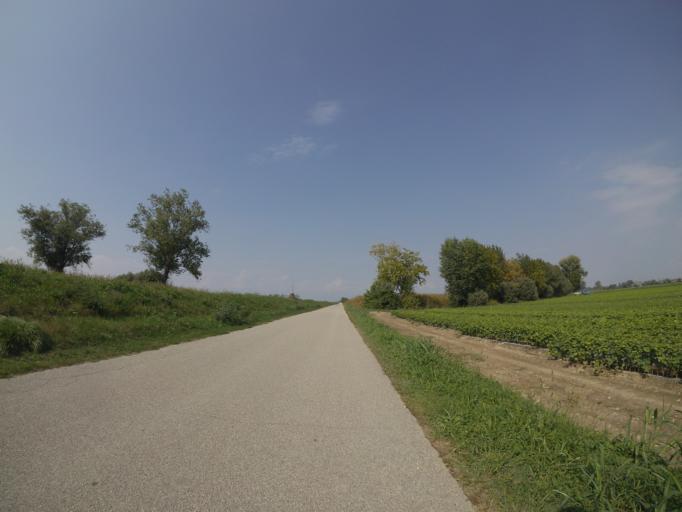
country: IT
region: Friuli Venezia Giulia
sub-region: Provincia di Udine
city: Camino al Tagliamento
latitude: 45.9210
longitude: 12.9255
